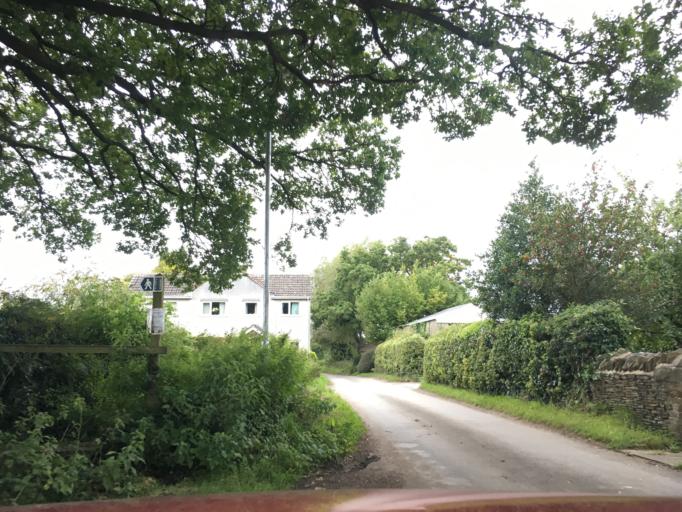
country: GB
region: England
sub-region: South Gloucestershire
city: Yate
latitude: 51.5484
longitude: -2.4416
